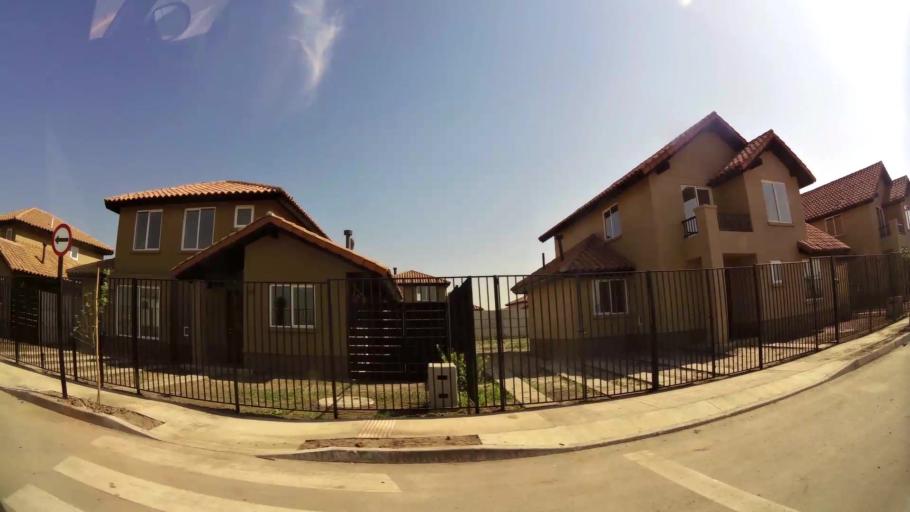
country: CL
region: Santiago Metropolitan
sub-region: Provincia de Talagante
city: Penaflor
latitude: -33.5667
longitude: -70.8299
